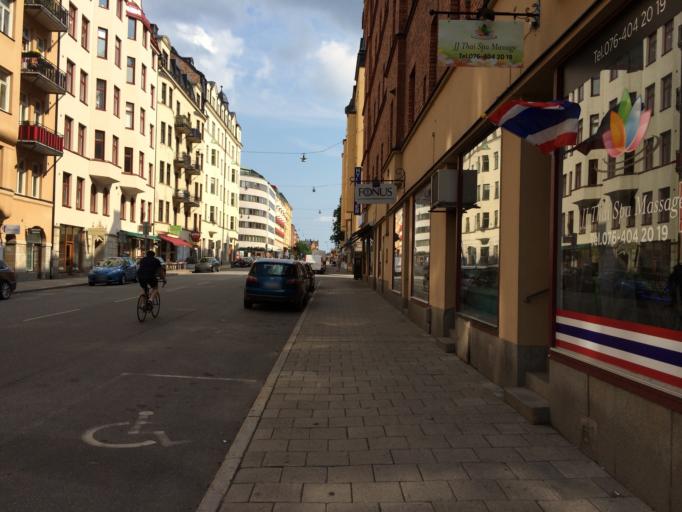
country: SE
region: Stockholm
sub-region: Stockholms Kommun
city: Stockholm
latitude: 59.3315
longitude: 18.0287
